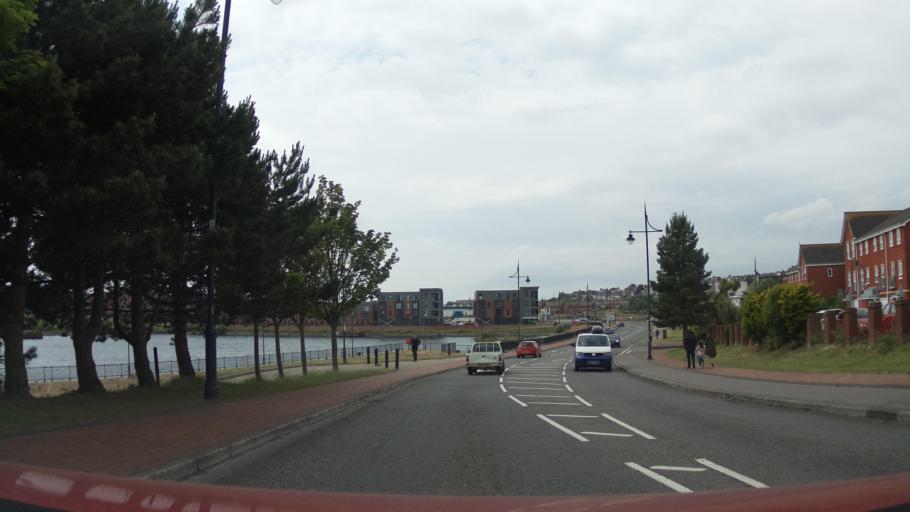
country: GB
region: Wales
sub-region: Vale of Glamorgan
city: Barry
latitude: 51.4000
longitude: -3.2743
